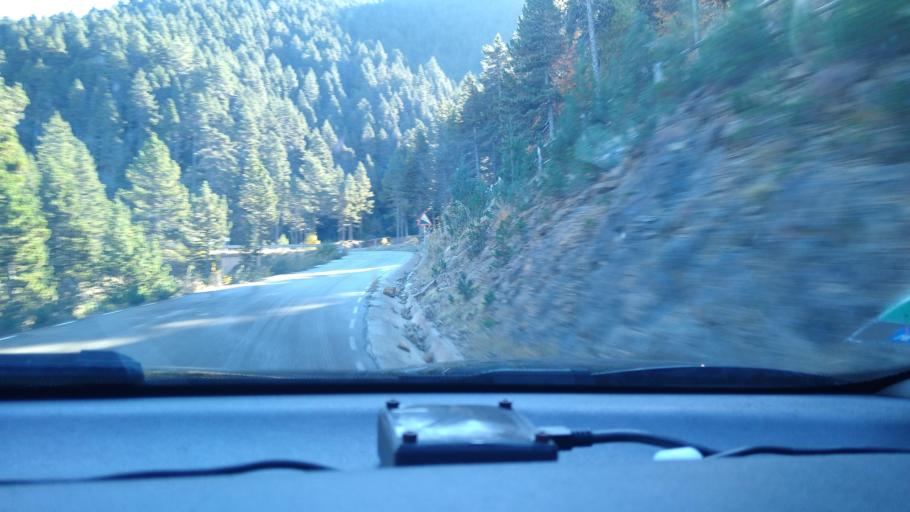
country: ES
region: Catalonia
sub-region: Provincia de Barcelona
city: Saldes
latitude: 42.1991
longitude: 1.7604
